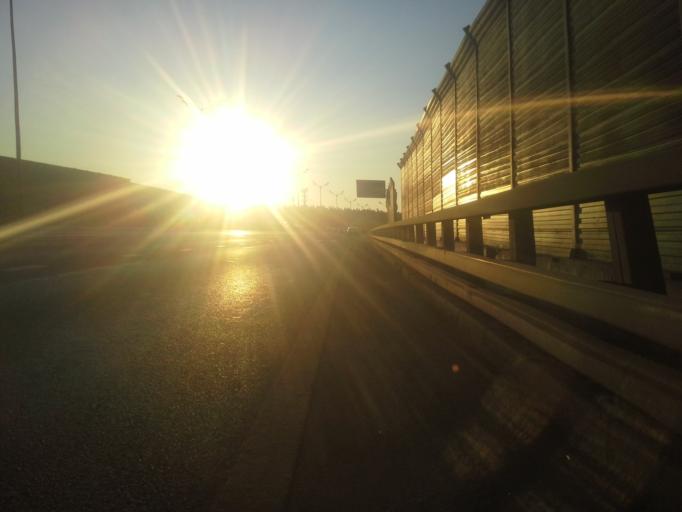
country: RU
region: Moskovskaya
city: Lesnoy Gorodok
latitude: 55.6299
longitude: 37.2066
